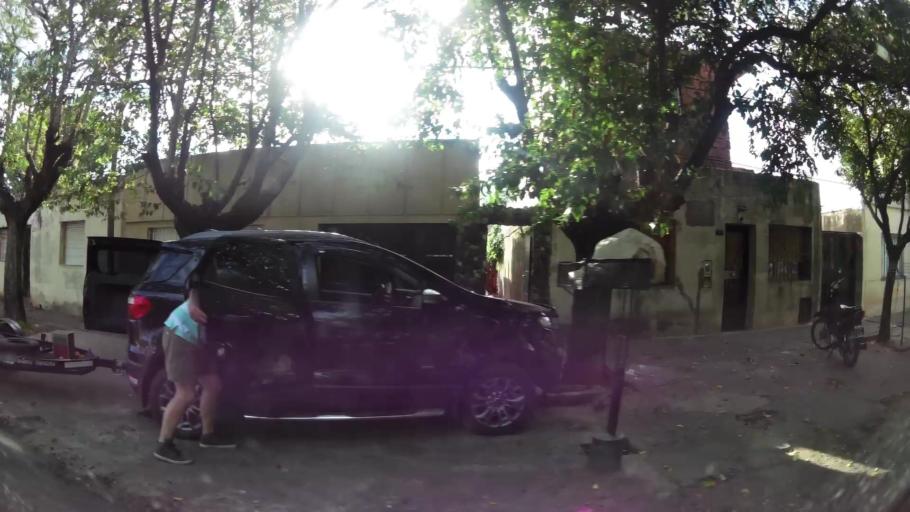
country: AR
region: Santa Fe
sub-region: Departamento de Rosario
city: Rosario
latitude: -32.9776
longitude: -60.6789
